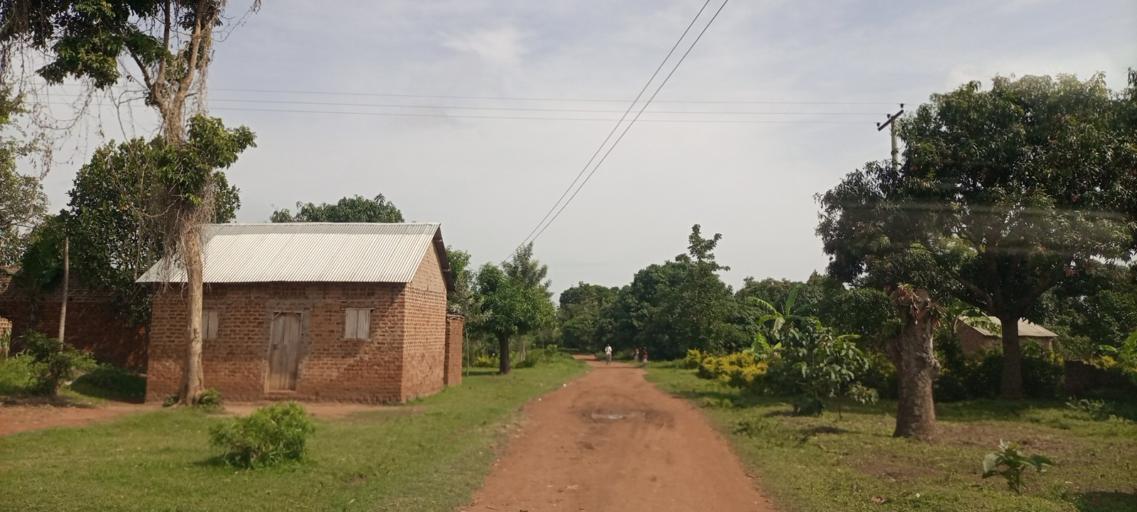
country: UG
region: Eastern Region
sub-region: Mbale District
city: Mbale
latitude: 1.1253
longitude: 34.0304
